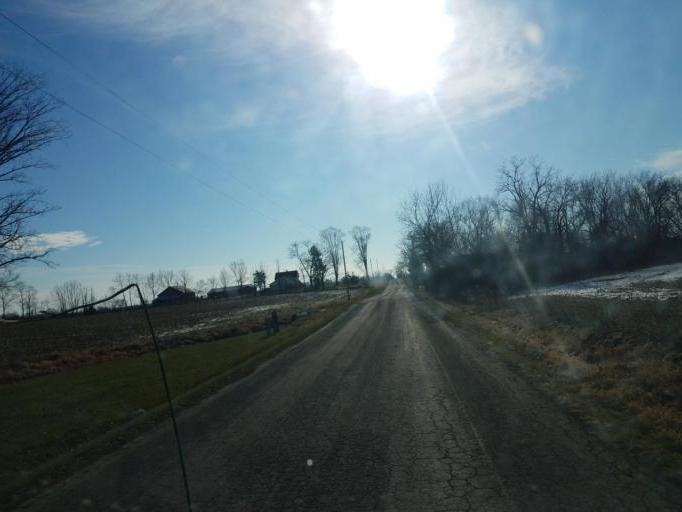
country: US
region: Ohio
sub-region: Morrow County
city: Cardington
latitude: 40.4812
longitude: -82.8692
